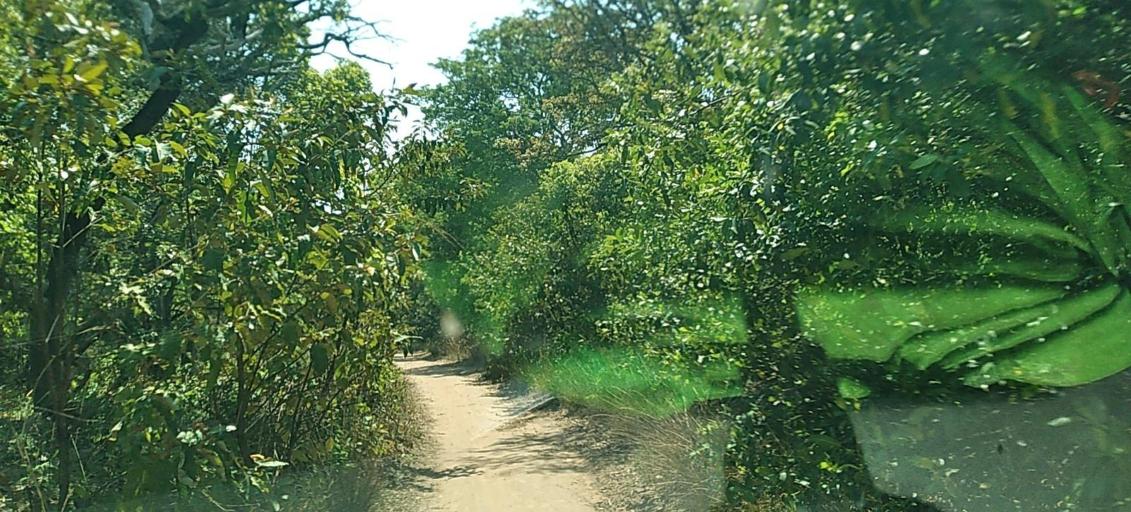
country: CD
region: Katanga
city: Kolwezi
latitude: -11.2760
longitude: 25.1138
